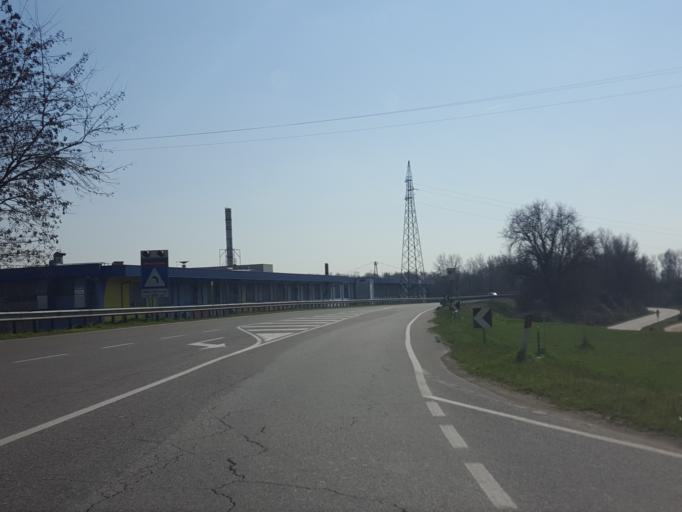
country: IT
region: Veneto
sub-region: Provincia di Padova
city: Fontaniva
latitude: 45.6347
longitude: 11.7385
